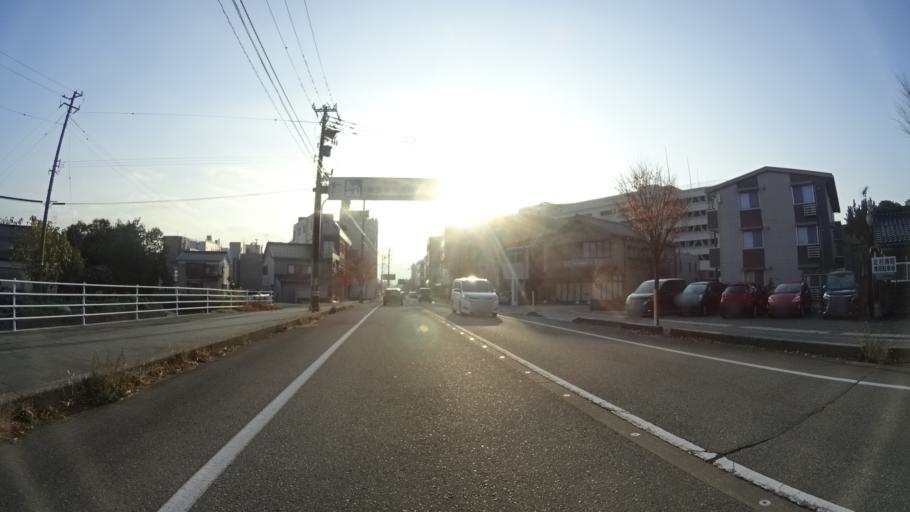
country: JP
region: Ishikawa
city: Nanao
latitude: 37.0446
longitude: 136.9622
